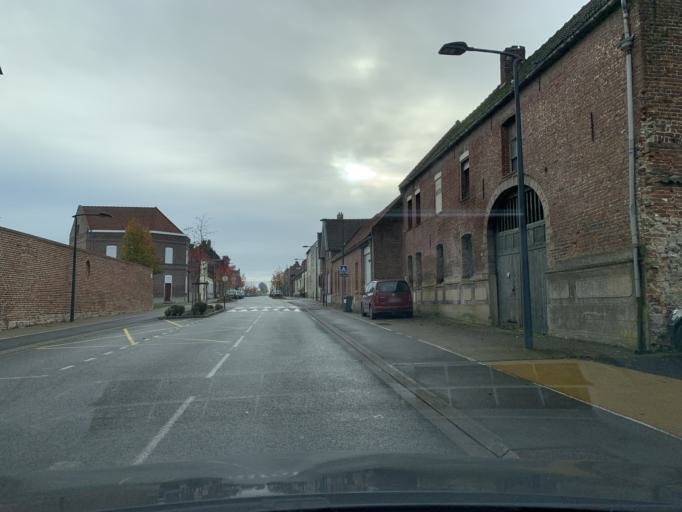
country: FR
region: Nord-Pas-de-Calais
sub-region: Departement du Nord
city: Cantin
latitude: 50.3095
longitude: 3.1275
